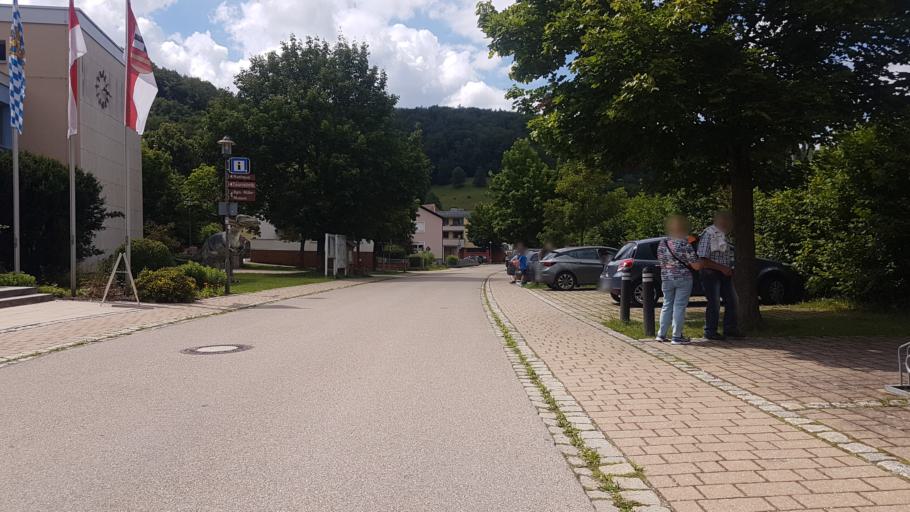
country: DE
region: Bavaria
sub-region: Regierungsbezirk Mittelfranken
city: Solnhofen
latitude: 48.8923
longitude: 10.9930
